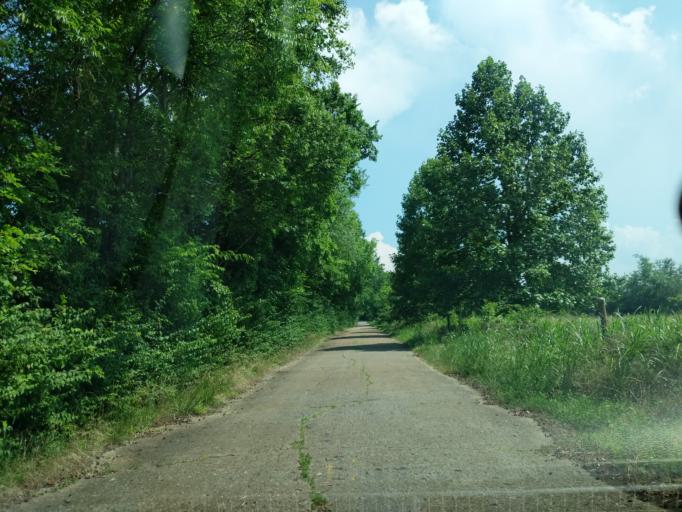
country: US
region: Tennessee
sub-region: Davidson County
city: Goodlettsville
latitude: 36.2881
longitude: -86.6805
